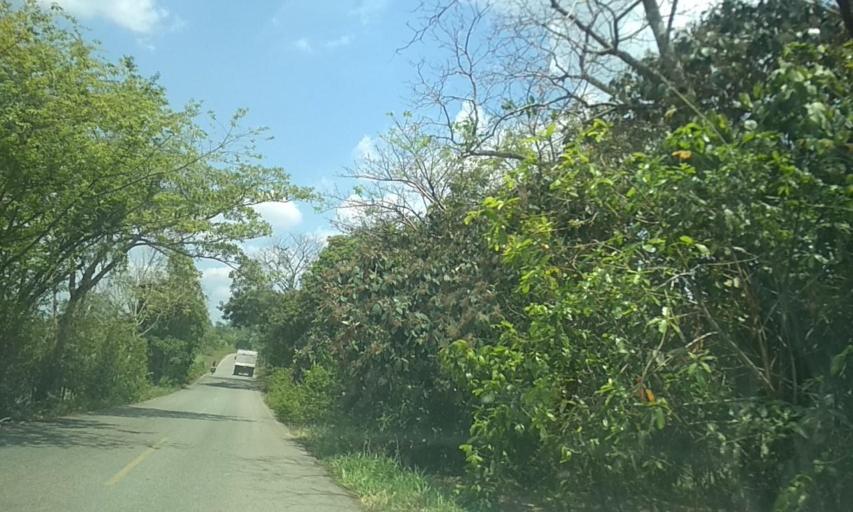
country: MX
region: Tabasco
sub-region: Huimanguillo
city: Francisco Rueda
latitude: 17.7734
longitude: -93.8091
